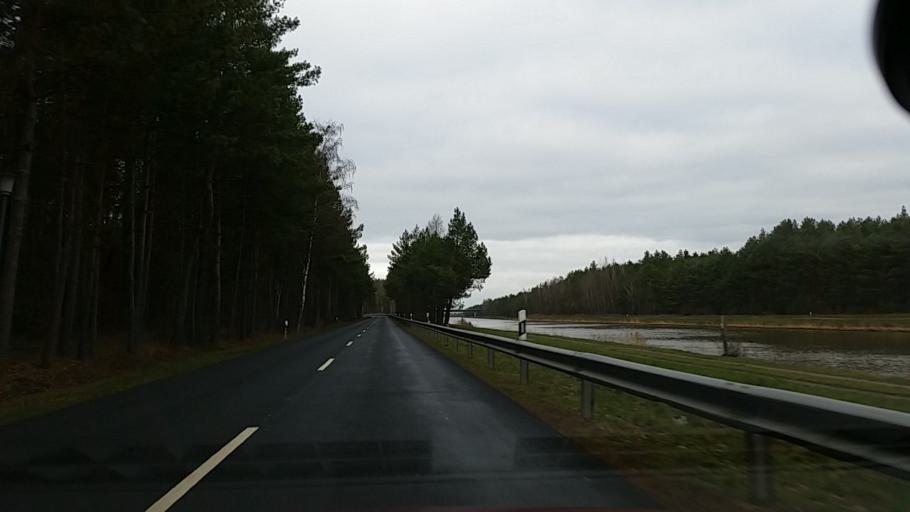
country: DE
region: Lower Saxony
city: Bodenteich
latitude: 52.8416
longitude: 10.6651
